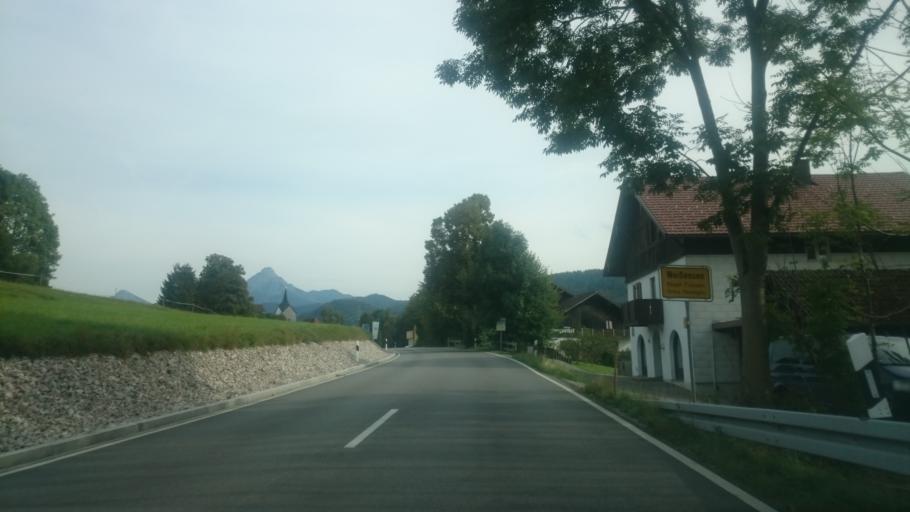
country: AT
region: Tyrol
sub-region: Politischer Bezirk Reutte
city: Vils
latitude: 47.5746
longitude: 10.6359
